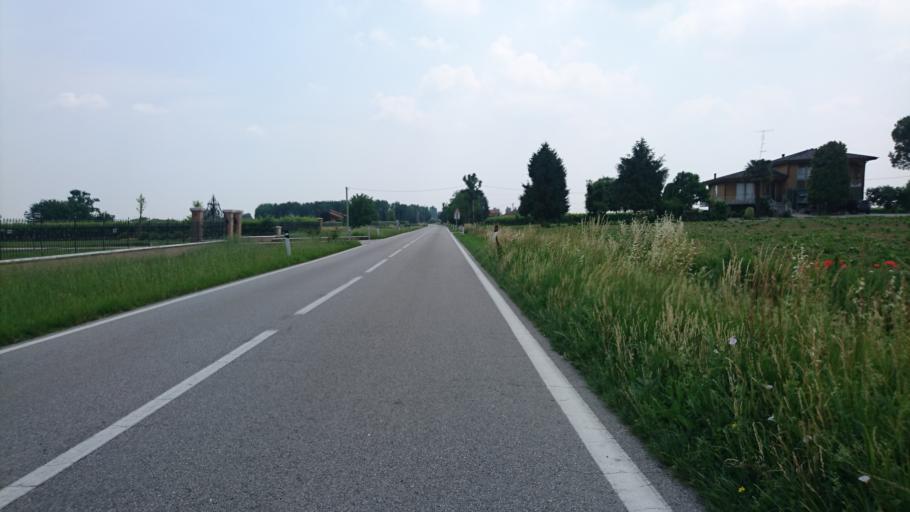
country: IT
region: Veneto
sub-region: Provincia di Padova
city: Terrassa Padovana
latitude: 45.2566
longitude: 11.8833
